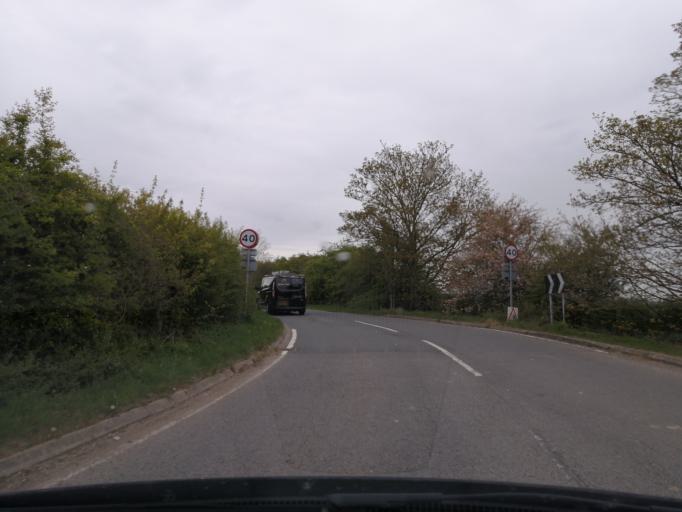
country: GB
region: England
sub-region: Peterborough
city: Wittering
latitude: 52.5923
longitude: -0.4586
